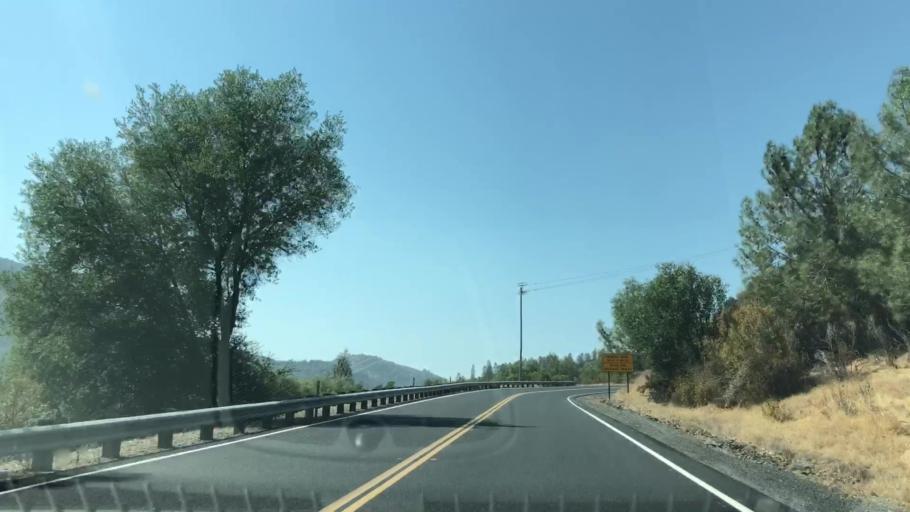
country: US
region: California
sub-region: Tuolumne County
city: Tuolumne City
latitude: 37.8168
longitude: -120.2989
